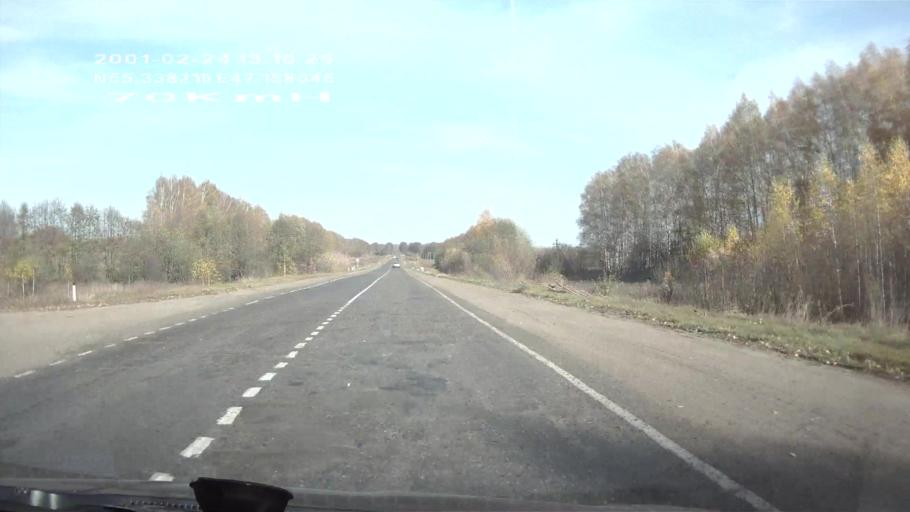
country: RU
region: Chuvashia
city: Ibresi
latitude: 55.3380
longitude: 47.1589
